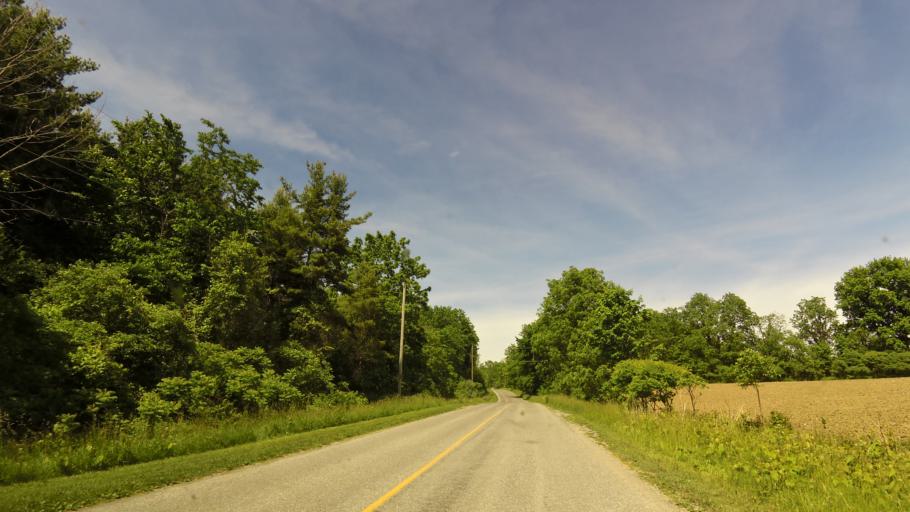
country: CA
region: Ontario
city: Norfolk County
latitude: 42.7246
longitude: -80.2955
